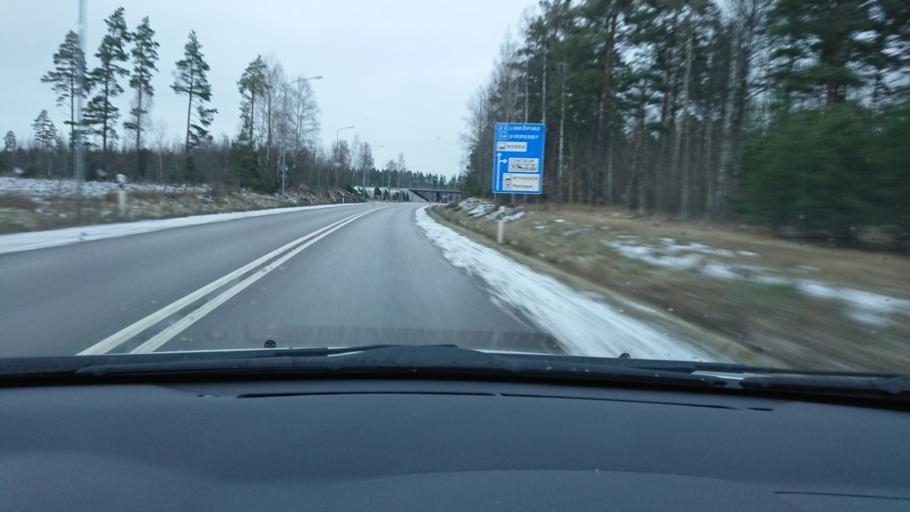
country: SE
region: Kalmar
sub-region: Hultsfreds Kommun
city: Hultsfred
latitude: 57.4982
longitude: 15.8209
